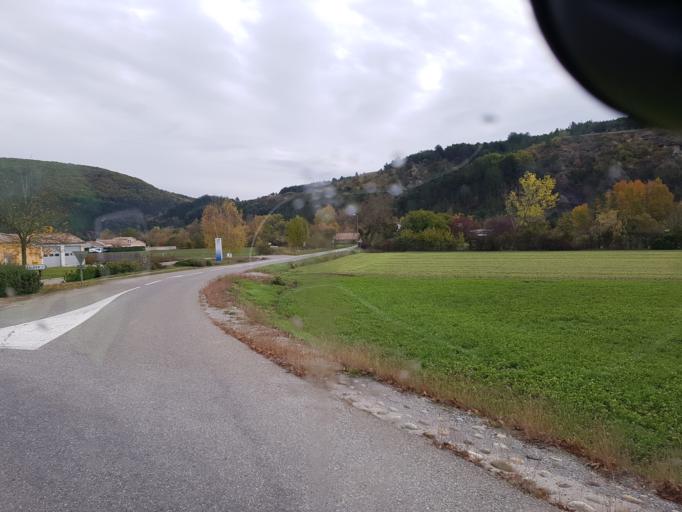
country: FR
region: Provence-Alpes-Cote d'Azur
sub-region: Departement des Hautes-Alpes
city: Laragne-Monteglin
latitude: 44.3412
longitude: 5.7634
